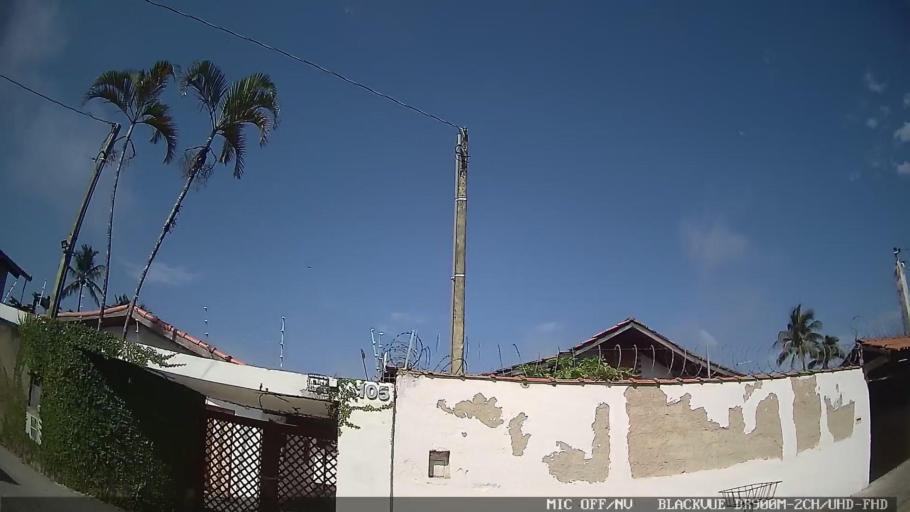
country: BR
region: Sao Paulo
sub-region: Guaruja
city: Guaruja
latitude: -23.9744
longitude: -46.1911
